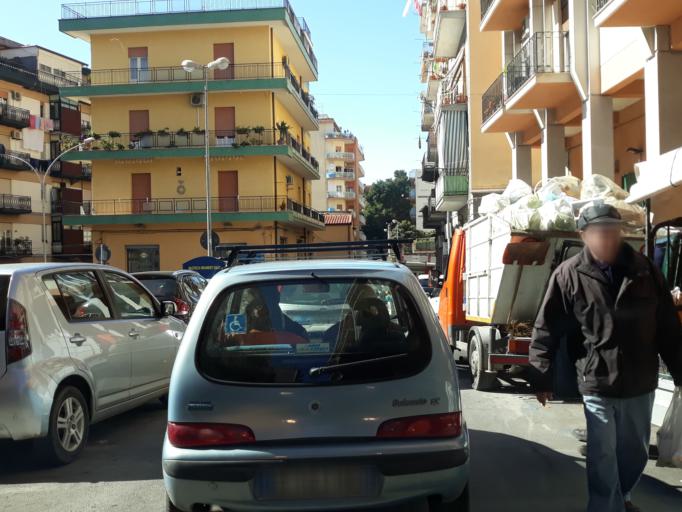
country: IT
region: Sicily
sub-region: Palermo
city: Monreale
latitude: 38.0786
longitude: 13.2847
